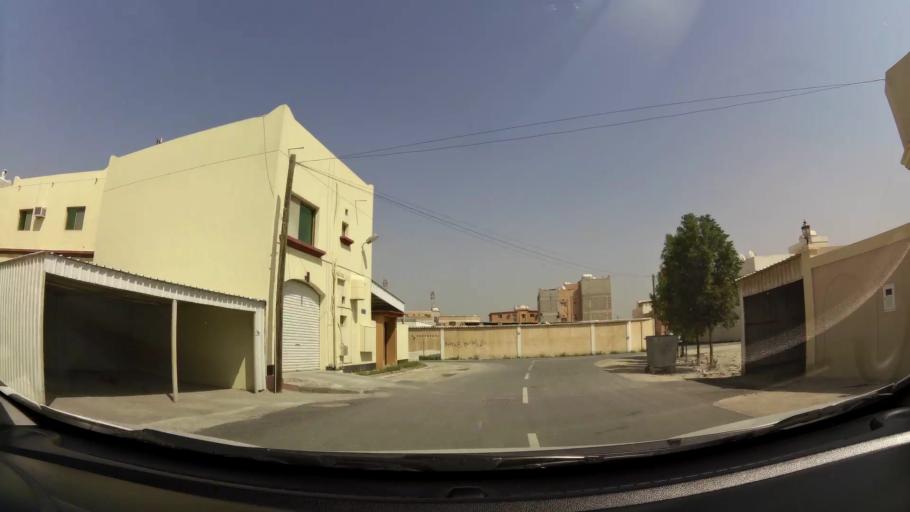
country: BH
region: Manama
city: Jidd Hafs
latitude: 26.2115
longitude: 50.4486
